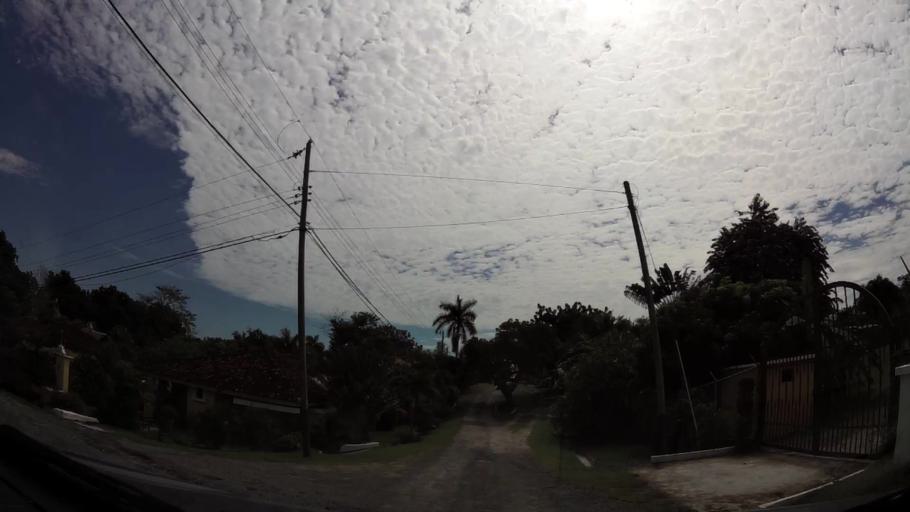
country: PA
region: Panama
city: Nueva Gorgona
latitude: 8.5402
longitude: -79.9051
